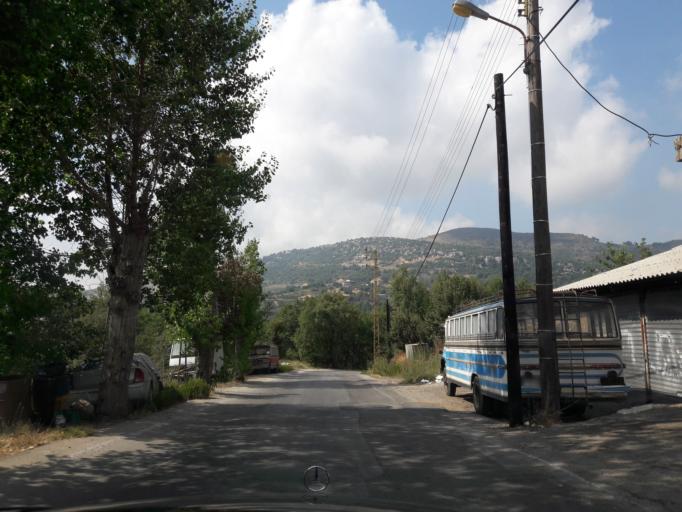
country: LB
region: Mont-Liban
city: Djounie
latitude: 33.9575
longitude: 35.7770
